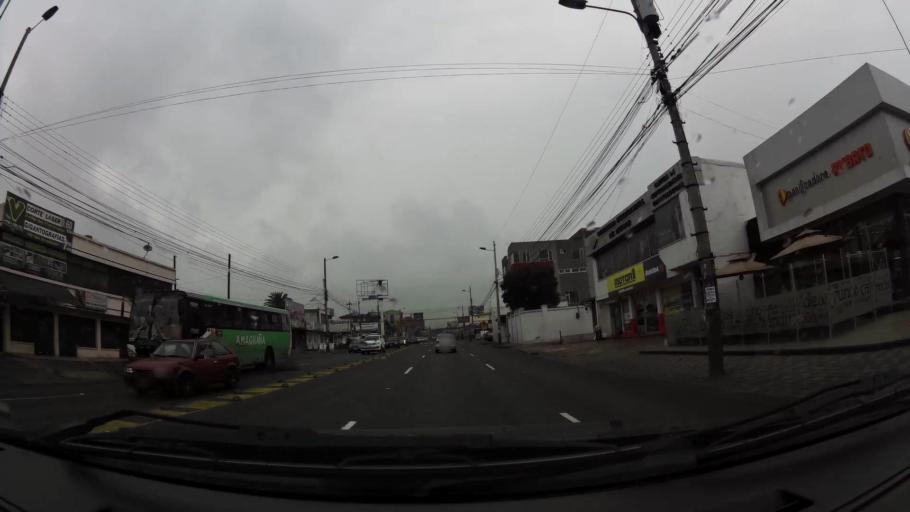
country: EC
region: Pichincha
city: Sangolqui
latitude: -0.2979
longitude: -78.4607
